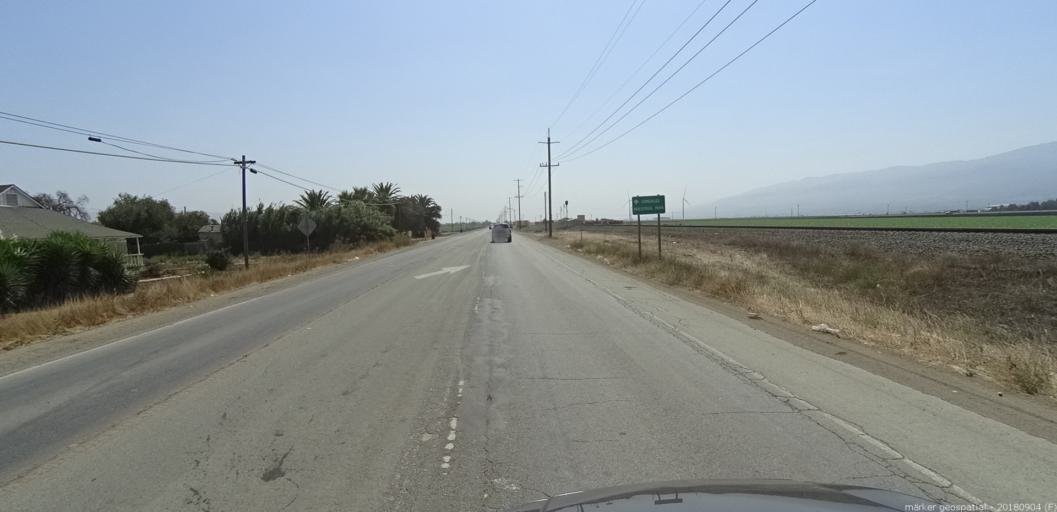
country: US
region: California
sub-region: Monterey County
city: Gonzales
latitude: 36.5210
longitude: -121.4628
